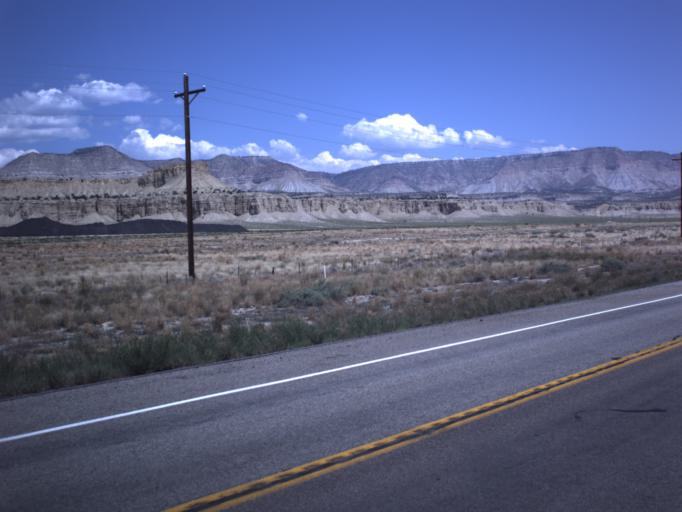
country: US
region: Utah
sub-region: Emery County
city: Ferron
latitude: 38.8550
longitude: -111.3052
